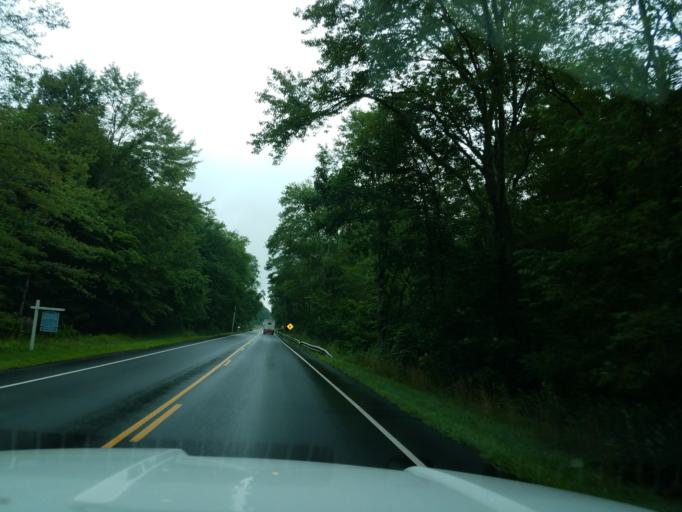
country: US
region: Connecticut
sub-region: New Haven County
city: Oxford
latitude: 41.4458
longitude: -73.1346
